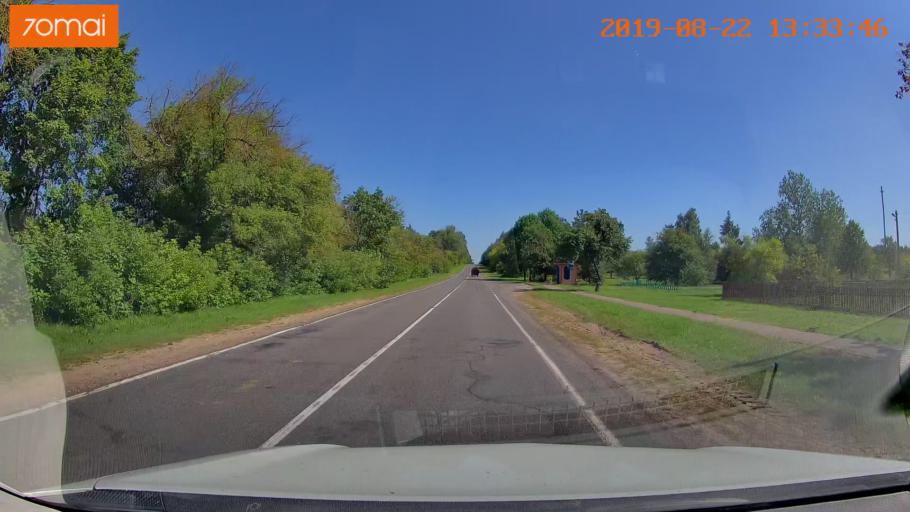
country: BY
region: Minsk
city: Staryya Darohi
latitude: 53.2161
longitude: 28.2290
